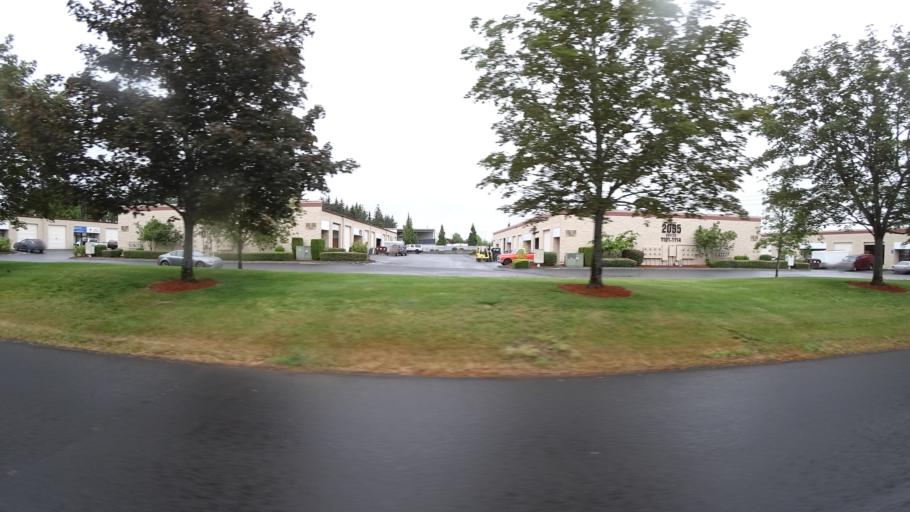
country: US
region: Oregon
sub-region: Washington County
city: Rockcreek
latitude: 45.5348
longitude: -122.8969
